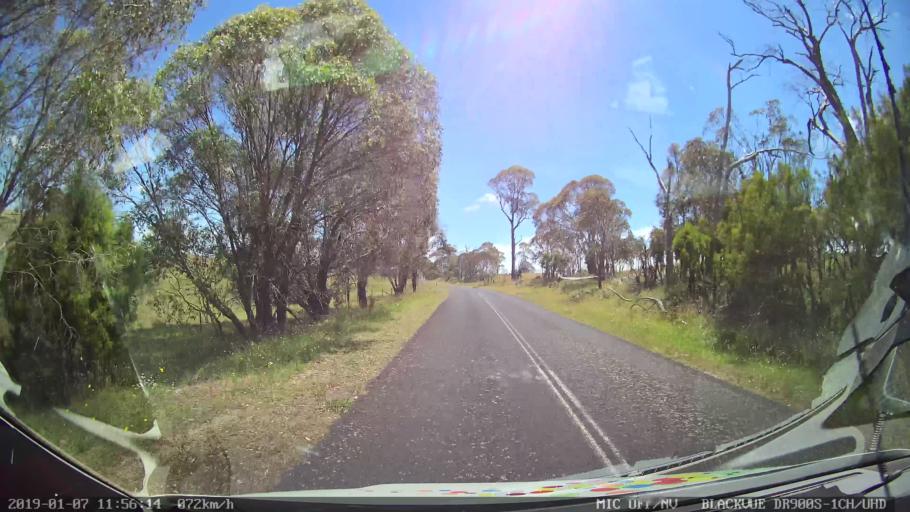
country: AU
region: New South Wales
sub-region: Guyra
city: Guyra
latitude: -30.2768
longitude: 151.6740
